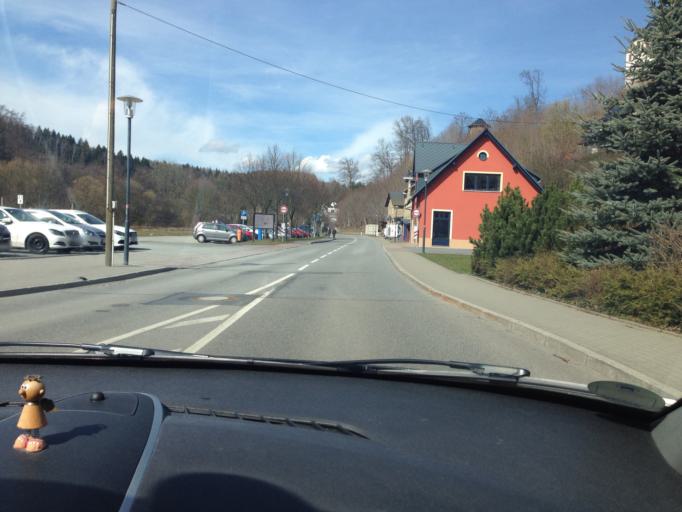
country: DE
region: Saxony
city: Scharfenstein
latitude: 50.7031
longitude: 13.0562
